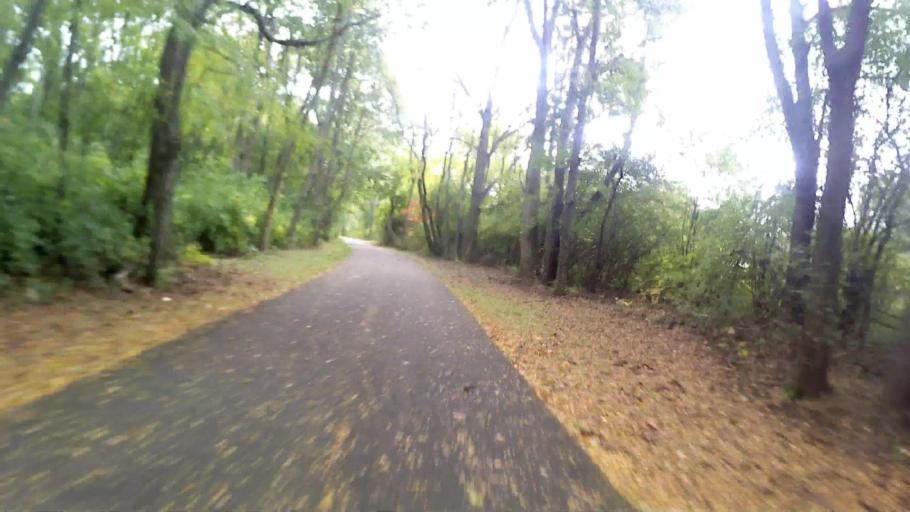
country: US
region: Illinois
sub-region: Kane County
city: Montgomery
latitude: 41.7505
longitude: -88.3742
